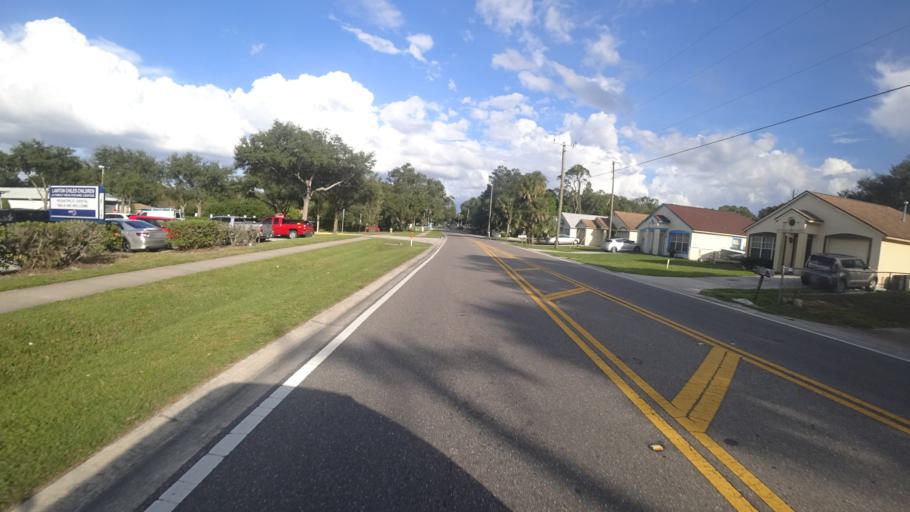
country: US
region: Florida
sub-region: Manatee County
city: Samoset
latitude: 27.4770
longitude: -82.5455
